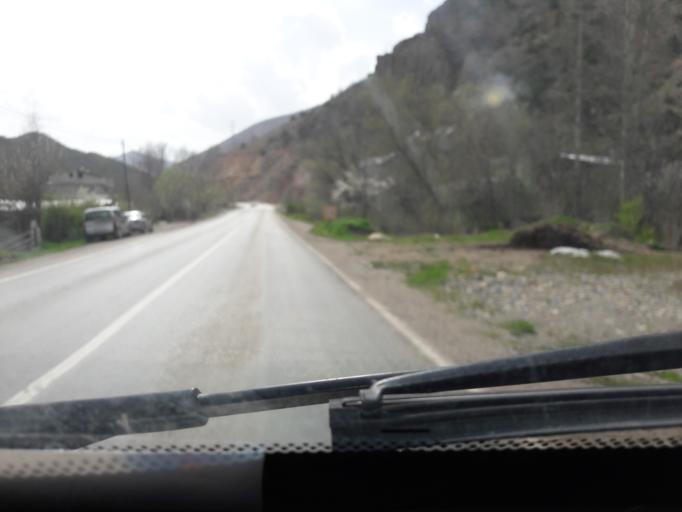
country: TR
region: Gumushane
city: Kale
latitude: 40.3963
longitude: 39.5998
